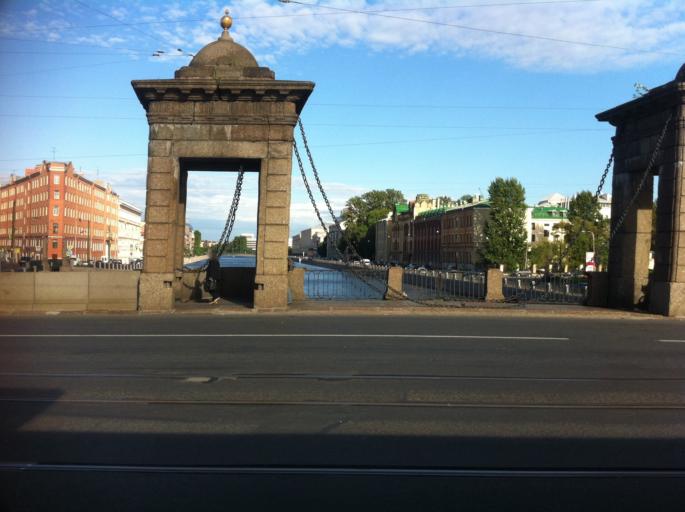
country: RU
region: St.-Petersburg
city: Admiralteisky
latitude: 59.9165
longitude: 30.2794
